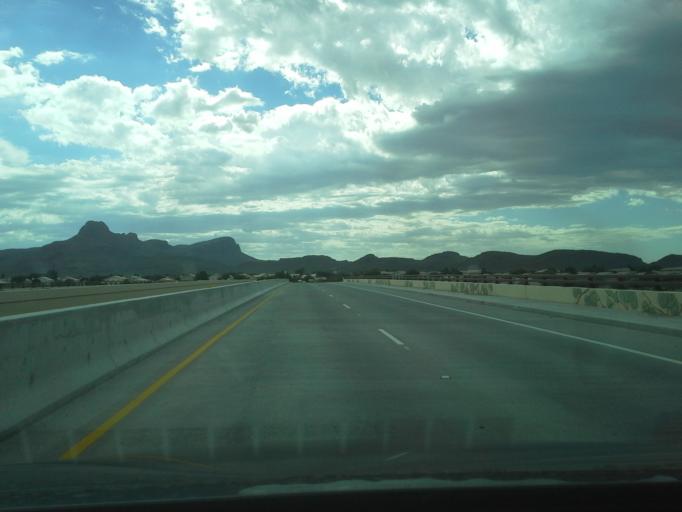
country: US
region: Arizona
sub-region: Pima County
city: Tortolita
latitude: 32.3764
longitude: -111.1144
